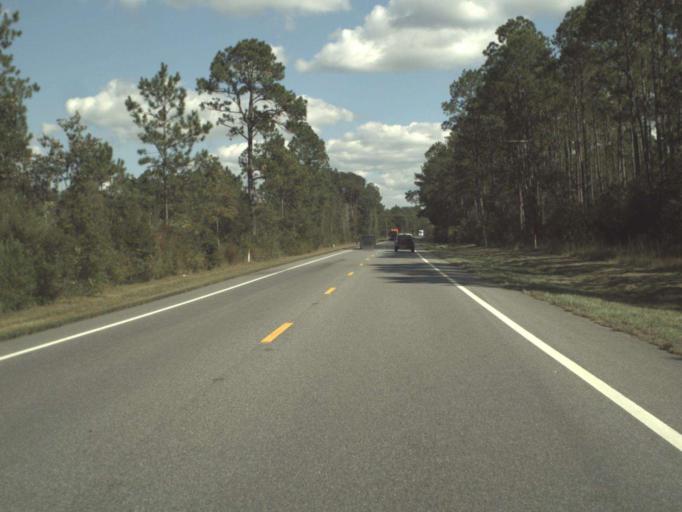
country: US
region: Florida
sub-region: Walton County
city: Freeport
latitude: 30.4732
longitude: -85.9752
